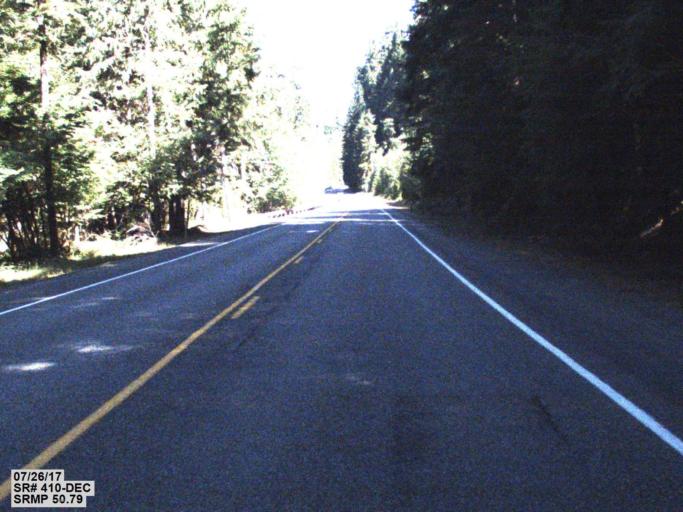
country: US
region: Washington
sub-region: King County
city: Enumclaw
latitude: 47.0619
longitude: -121.5753
